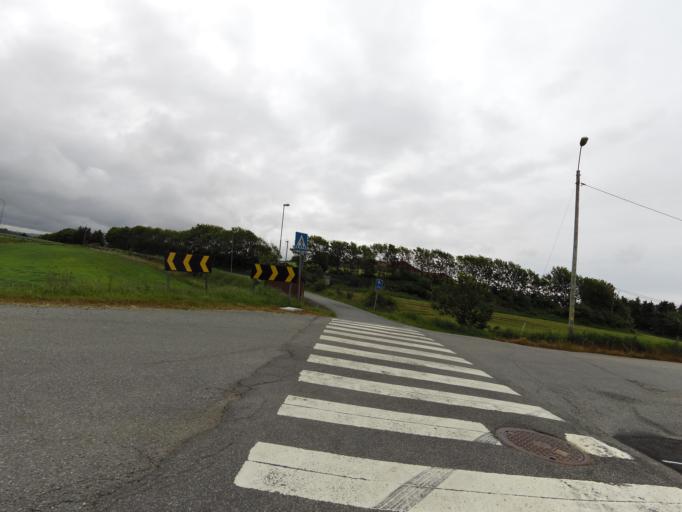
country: NO
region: Rogaland
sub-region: Klepp
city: Kleppe
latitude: 58.8206
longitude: 5.5875
